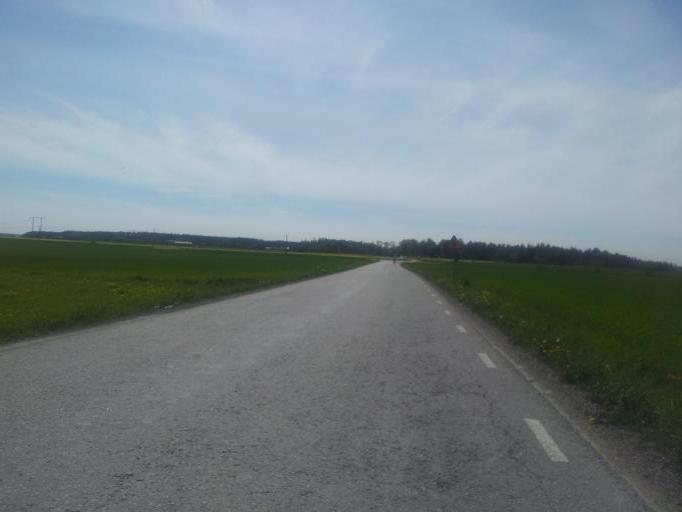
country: SE
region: Uppsala
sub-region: Uppsala Kommun
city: Saevja
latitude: 59.8494
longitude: 17.7382
